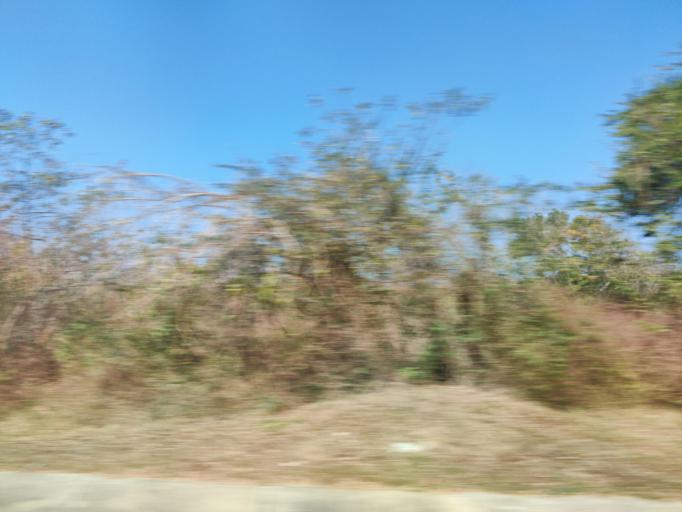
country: CO
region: Atlantico
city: Piojo
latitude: 10.7474
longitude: -75.2512
